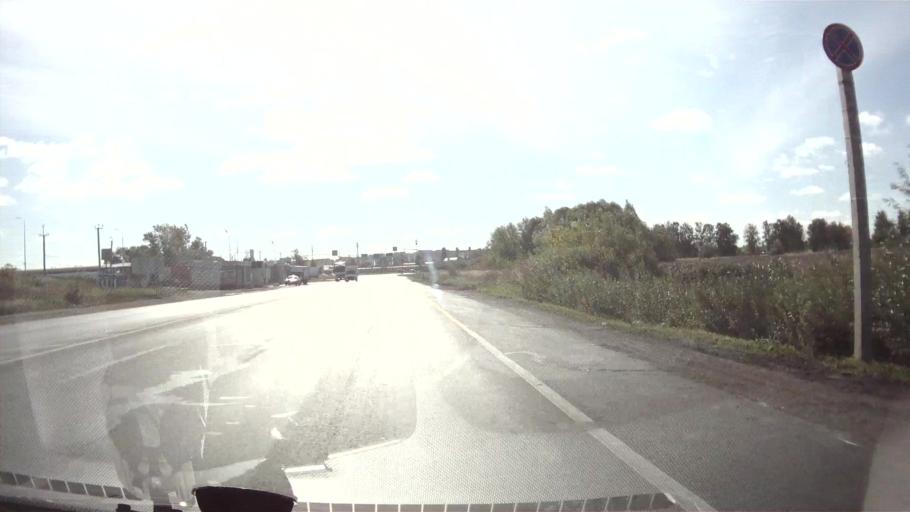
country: RU
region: Ulyanovsk
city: Isheyevka
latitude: 54.2942
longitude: 48.2513
